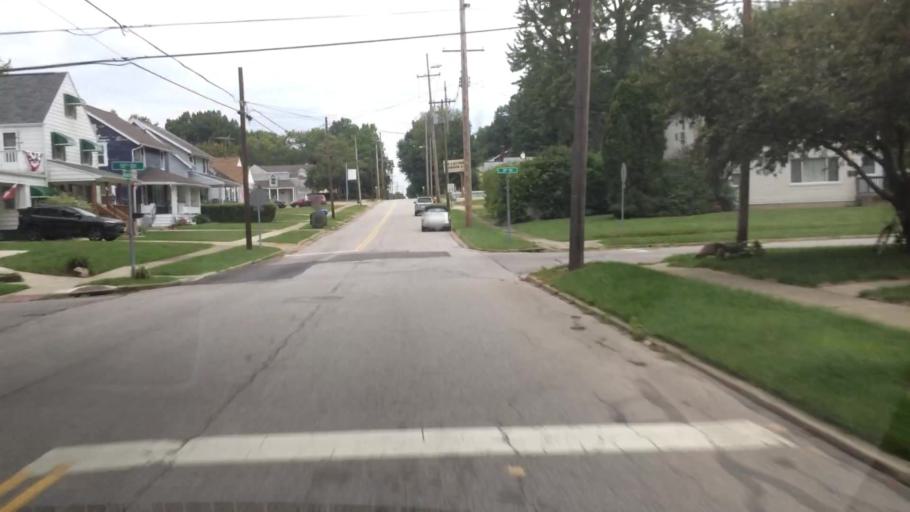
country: US
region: Ohio
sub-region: Summit County
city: Cuyahoga Falls
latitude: 41.1312
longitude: -81.4961
